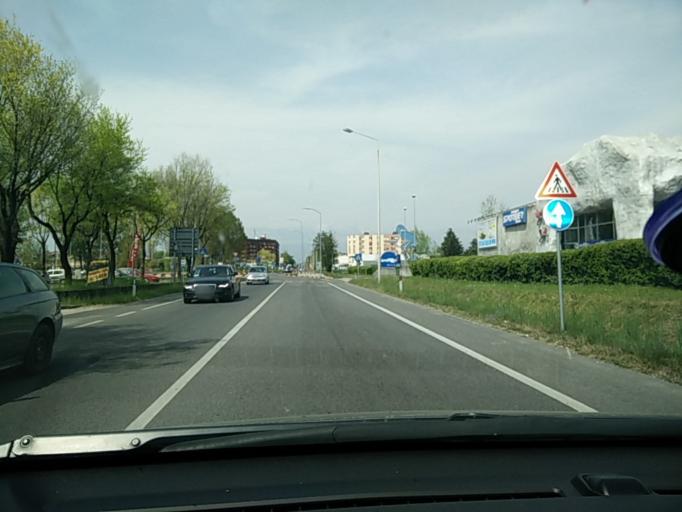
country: IT
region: Friuli Venezia Giulia
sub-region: Provincia di Pordenone
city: Pordenone
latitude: 45.9623
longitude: 12.6757
